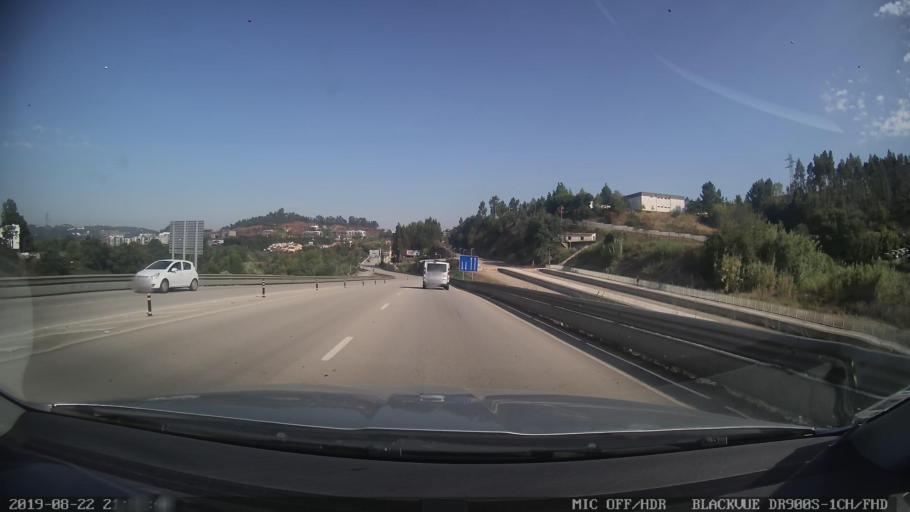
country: PT
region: Coimbra
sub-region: Coimbra
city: Coimbra
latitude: 40.1814
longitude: -8.3931
